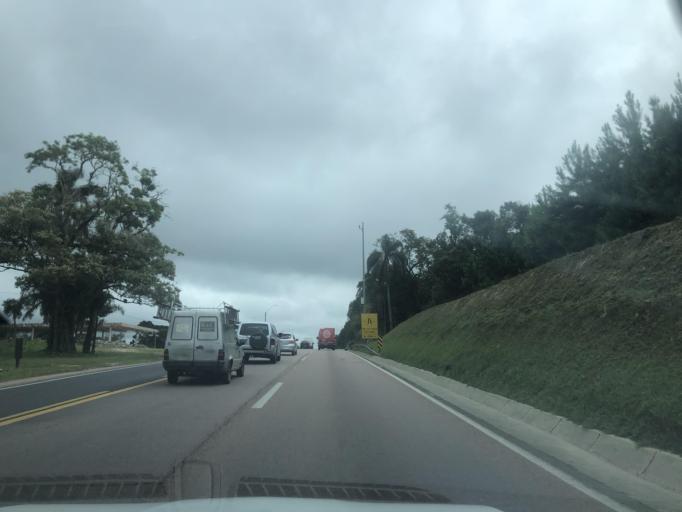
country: BR
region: Parana
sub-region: Araucaria
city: Araucaria
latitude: -25.8360
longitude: -49.3402
